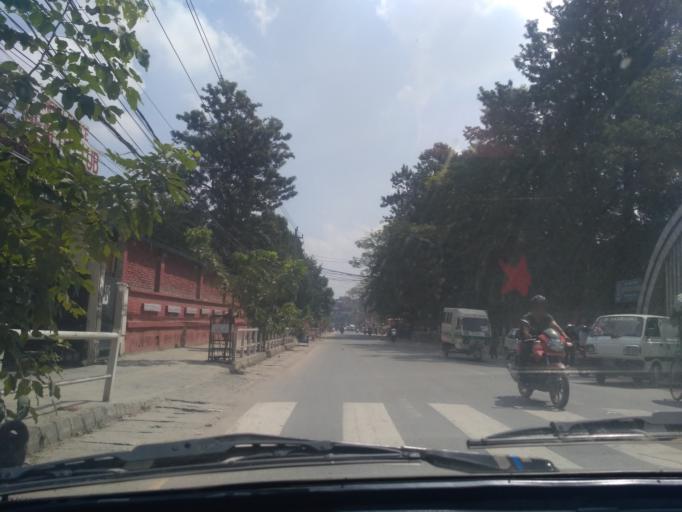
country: NP
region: Central Region
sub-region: Bagmati Zone
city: Kathmandu
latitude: 27.7022
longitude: 85.3180
